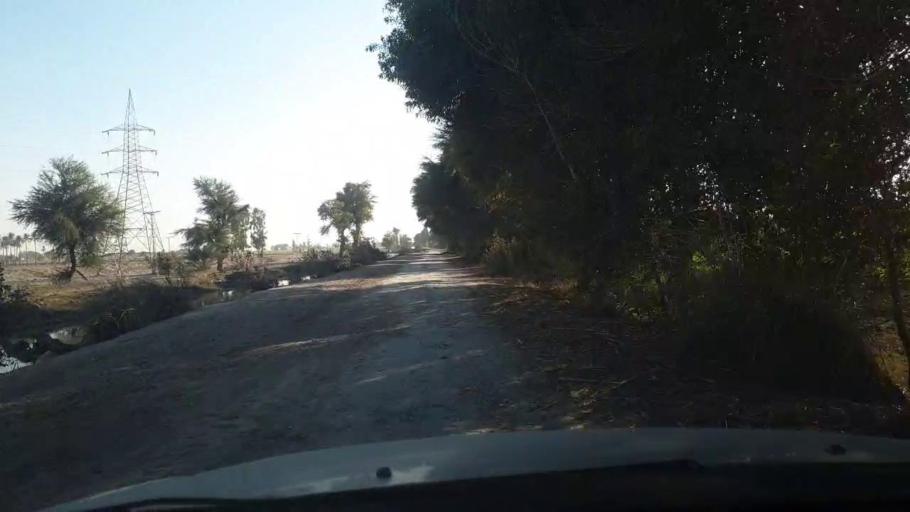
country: PK
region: Sindh
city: Ghotki
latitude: 28.0373
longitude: 69.3239
